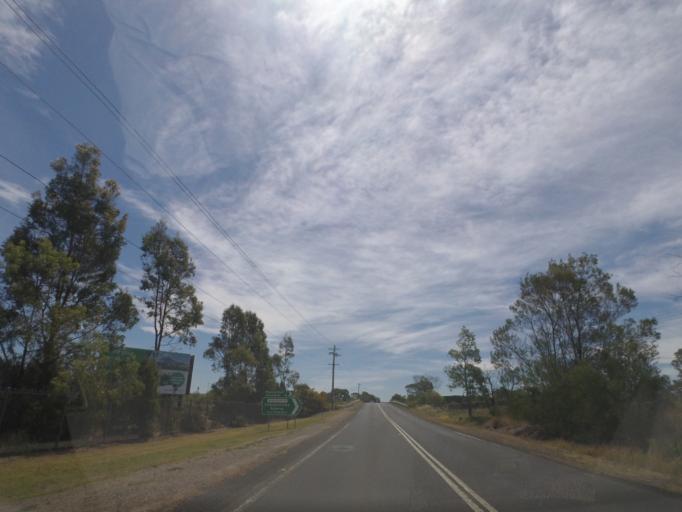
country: AU
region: New South Wales
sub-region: Wollondilly
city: Buxton
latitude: -34.2965
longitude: 150.5841
